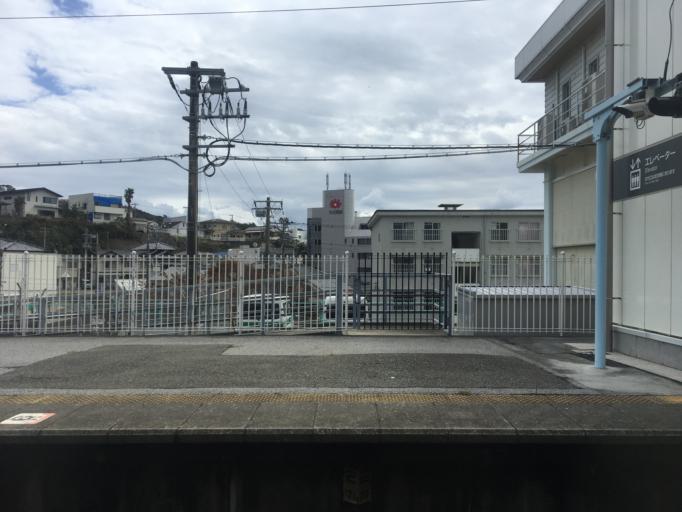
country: JP
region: Chiba
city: Katsuura
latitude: 35.1532
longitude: 140.3131
